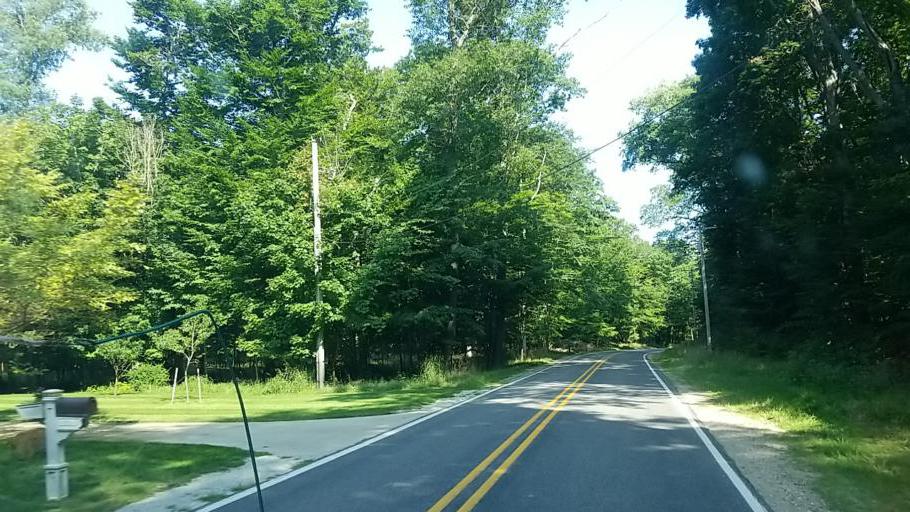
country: US
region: Michigan
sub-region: Muskegon County
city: Whitehall
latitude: 43.3258
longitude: -86.3984
